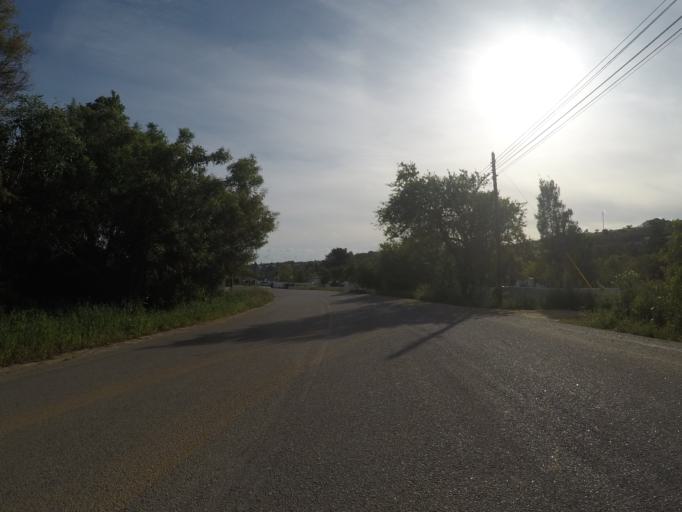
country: PT
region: Faro
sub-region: Lagos
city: Lagos
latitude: 37.1005
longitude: -8.7160
